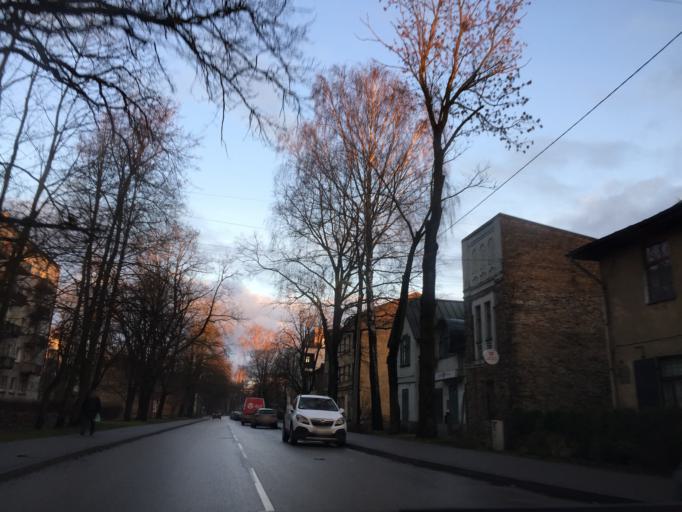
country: LV
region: Marupe
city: Marupe
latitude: 56.9363
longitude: 24.0412
